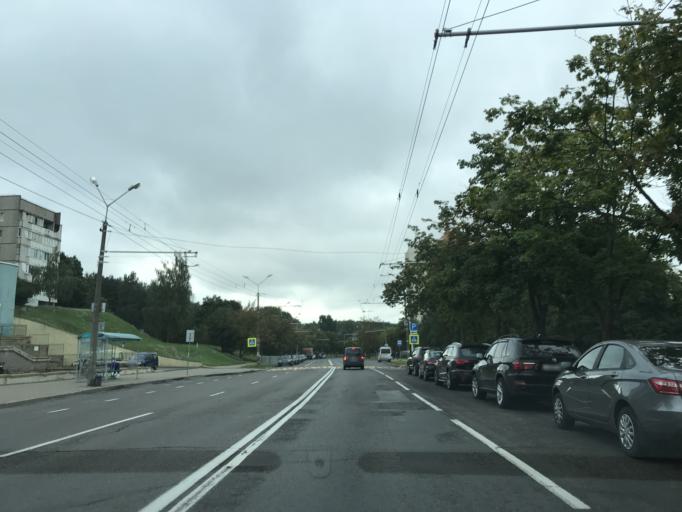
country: BY
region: Minsk
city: Borovlyany
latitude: 53.9509
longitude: 27.6367
